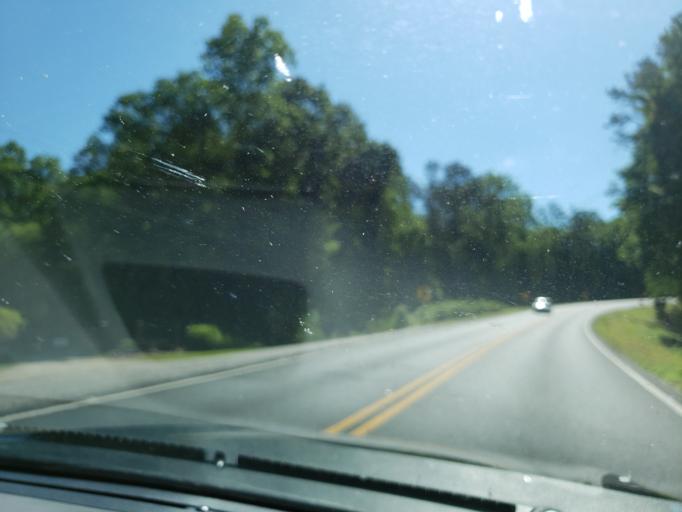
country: US
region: Alabama
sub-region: Calhoun County
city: Choccolocco
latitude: 33.5907
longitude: -85.6871
